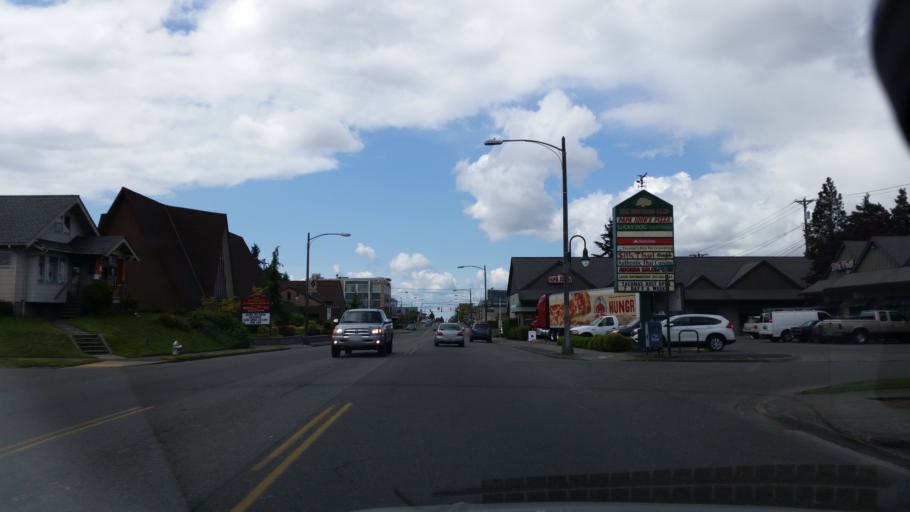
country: US
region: Washington
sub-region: Pierce County
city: Tacoma
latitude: 47.2553
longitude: -122.4803
